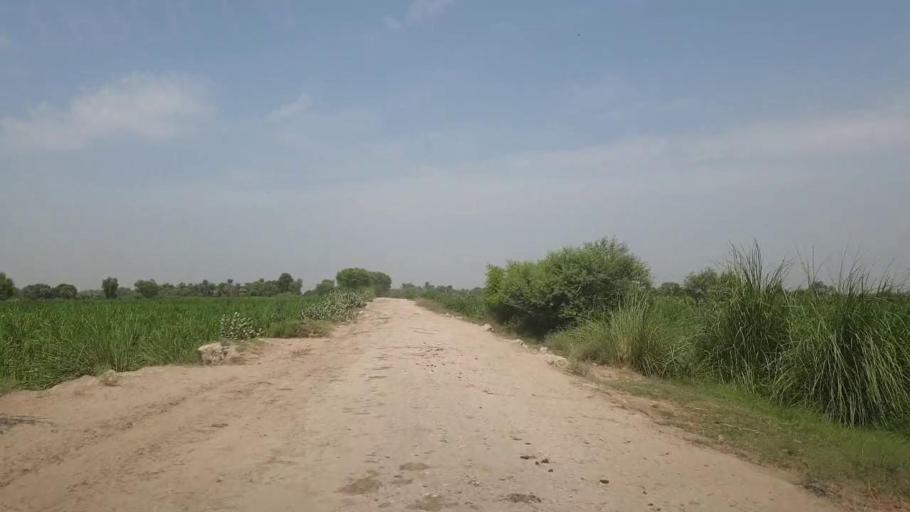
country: PK
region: Sindh
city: Pir jo Goth
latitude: 27.5481
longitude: 68.5140
